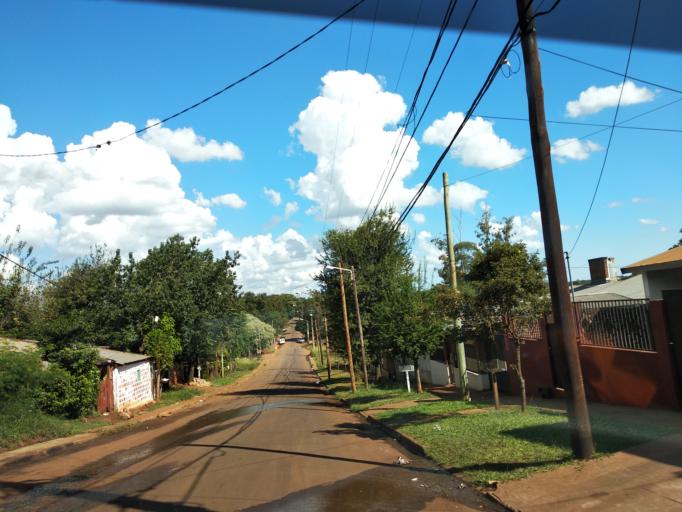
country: AR
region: Misiones
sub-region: Departamento de Capital
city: Posadas
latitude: -27.3862
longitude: -55.9458
